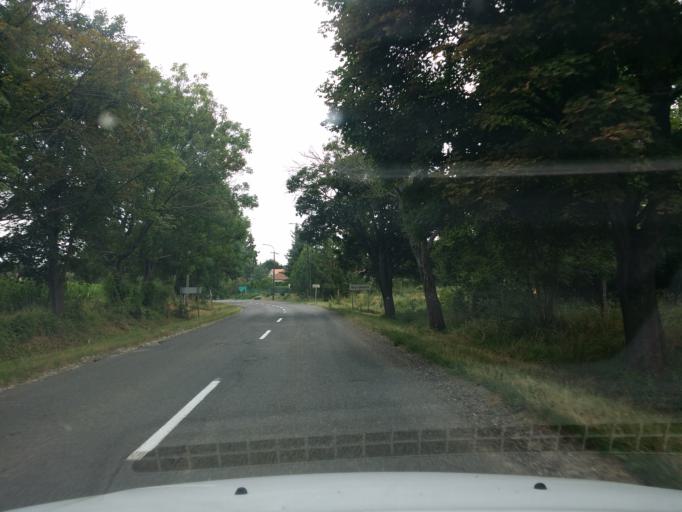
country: HU
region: Nograd
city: Bercel
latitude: 47.8888
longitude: 19.3687
